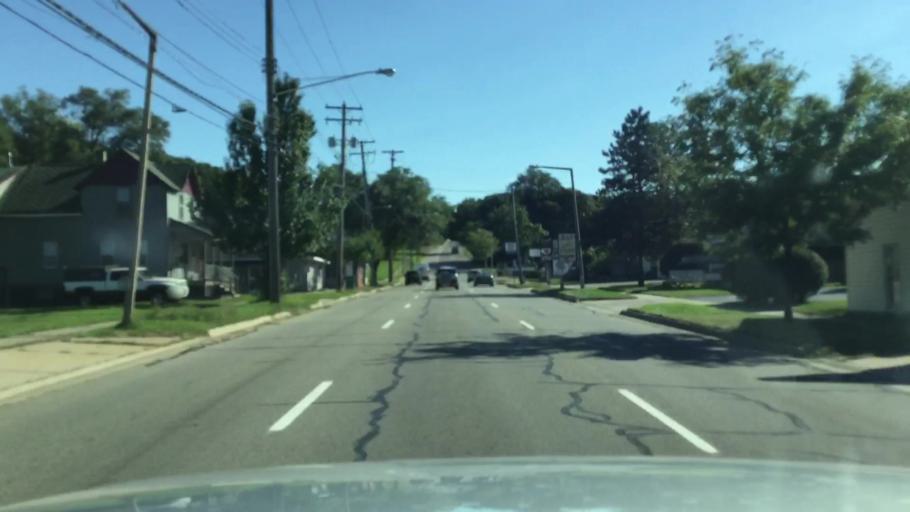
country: US
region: Michigan
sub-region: Kalamazoo County
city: Kalamazoo
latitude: 42.2740
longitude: -85.5896
